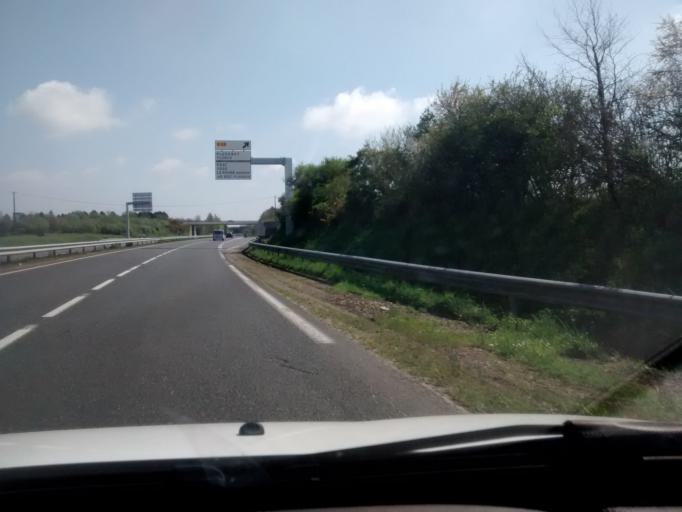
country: FR
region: Brittany
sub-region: Departement des Cotes-d'Armor
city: Cavan
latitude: 48.6606
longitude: -3.3395
